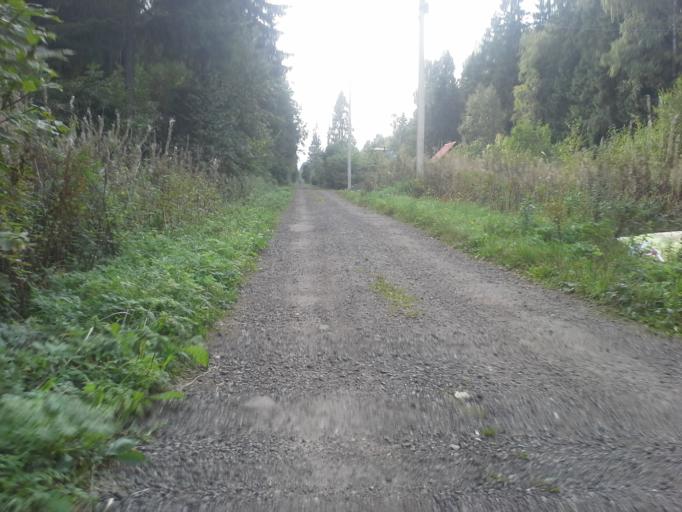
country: RU
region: Moskovskaya
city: Aprelevka
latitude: 55.5684
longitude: 37.0875
